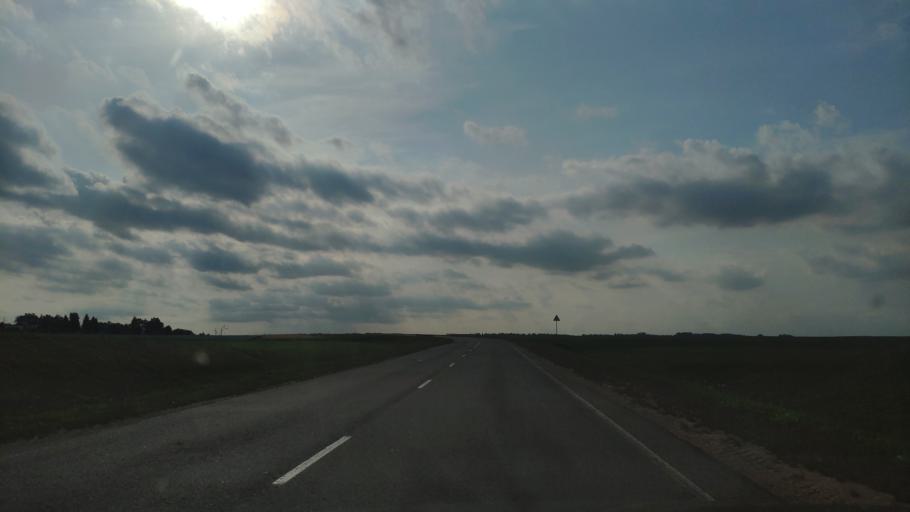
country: BY
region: Minsk
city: Azyartso
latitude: 53.8360
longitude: 27.3418
